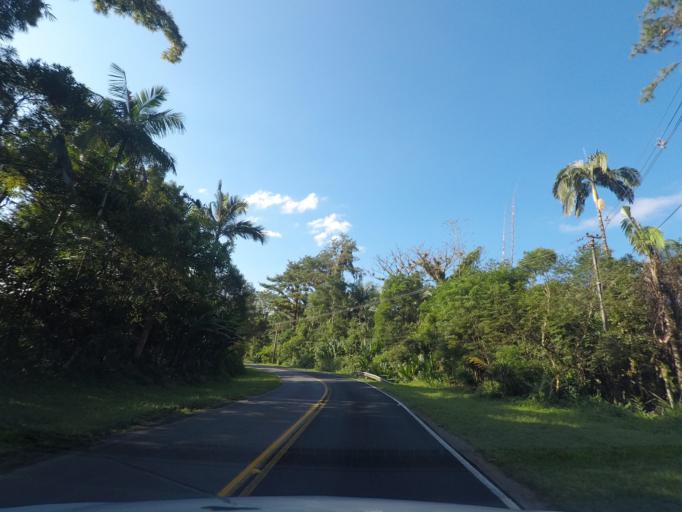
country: BR
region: Parana
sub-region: Antonina
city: Antonina
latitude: -25.4231
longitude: -48.8756
